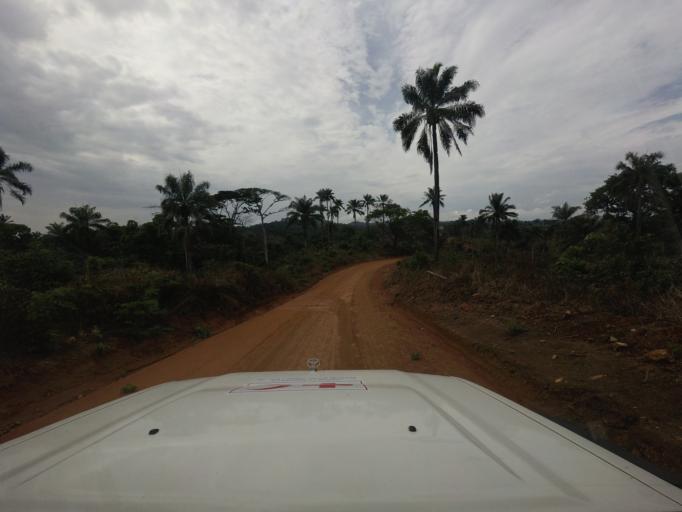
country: SL
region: Eastern Province
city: Buedu
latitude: 8.2207
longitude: -10.2220
